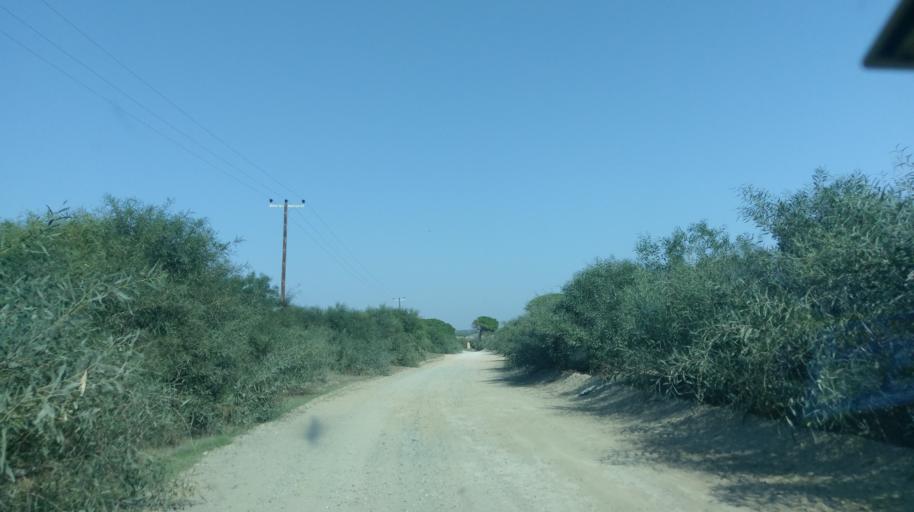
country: CY
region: Lefkosia
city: Morfou
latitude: 35.2884
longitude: 32.9481
